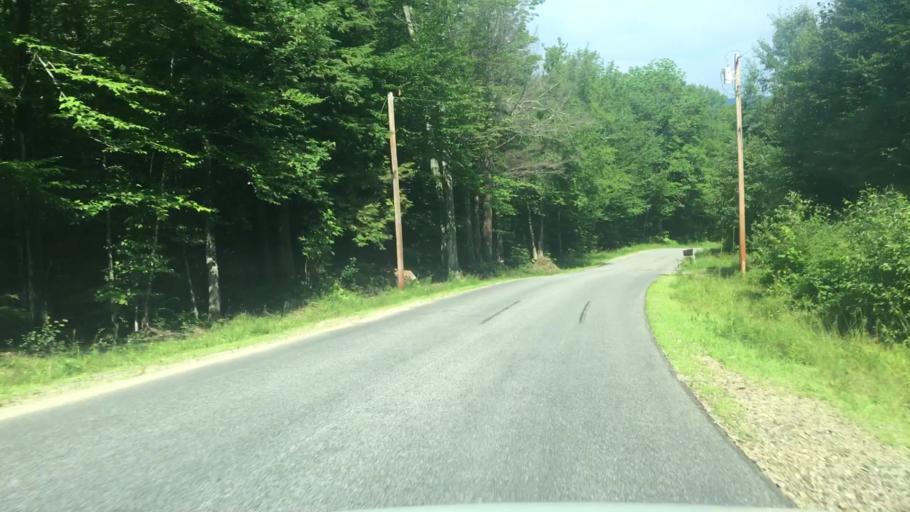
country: US
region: Maine
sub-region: Oxford County
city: West Paris
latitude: 44.3276
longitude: -70.5123
